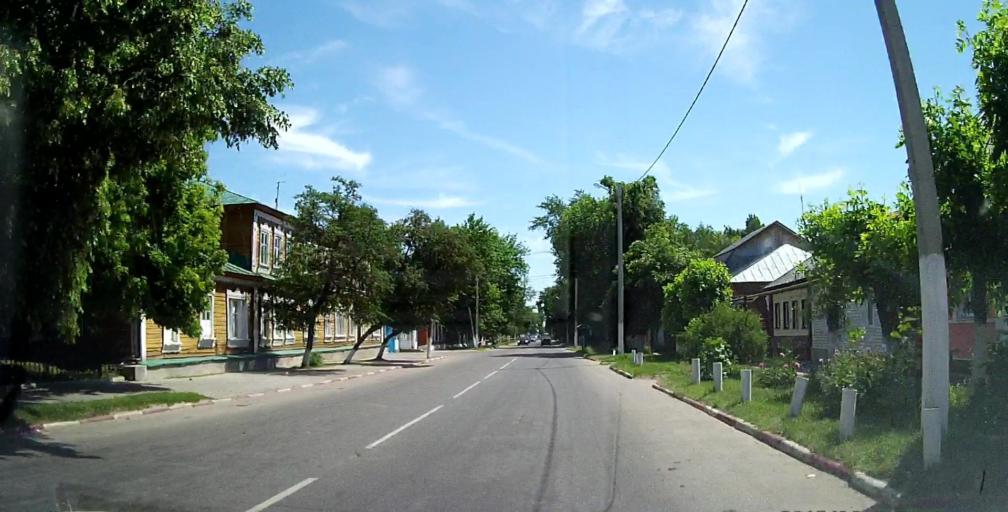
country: RU
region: Lipetsk
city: Chaplygin
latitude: 53.2424
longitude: 39.9653
